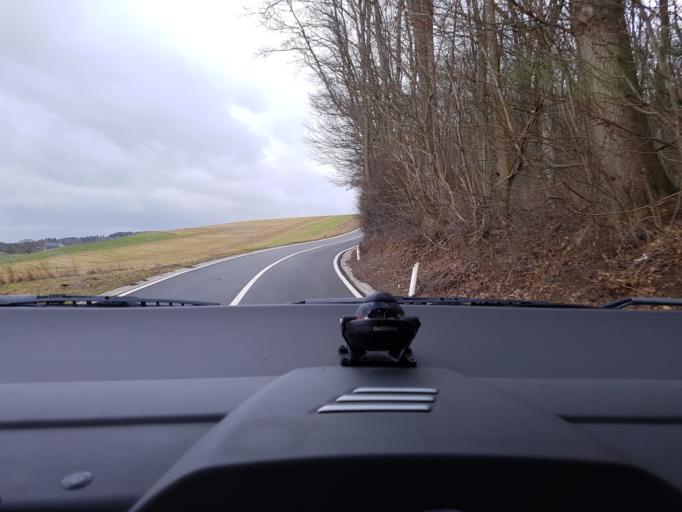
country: BE
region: Wallonia
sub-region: Province de Namur
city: Ciney
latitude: 50.2831
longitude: 5.1476
